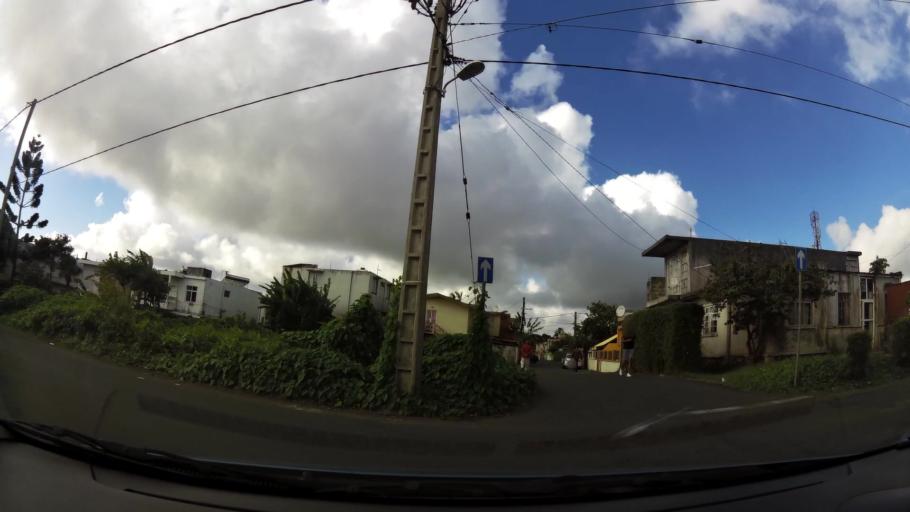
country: MU
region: Plaines Wilhems
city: Curepipe
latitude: -20.3264
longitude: 57.5227
